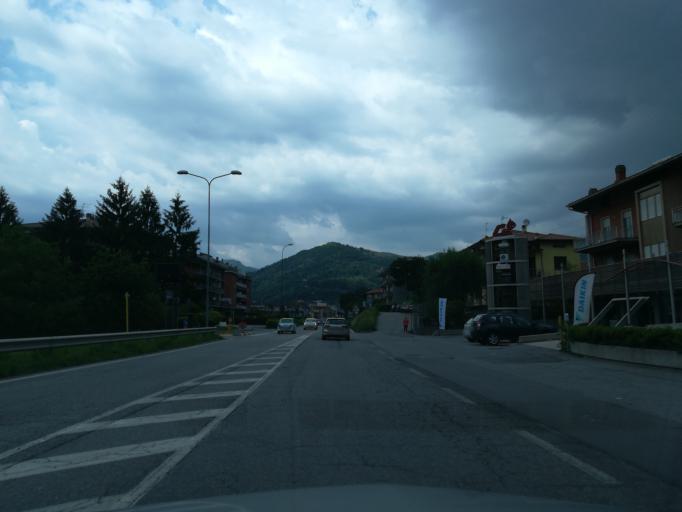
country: IT
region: Lombardy
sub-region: Provincia di Bergamo
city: Alme
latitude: 45.7400
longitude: 9.6095
